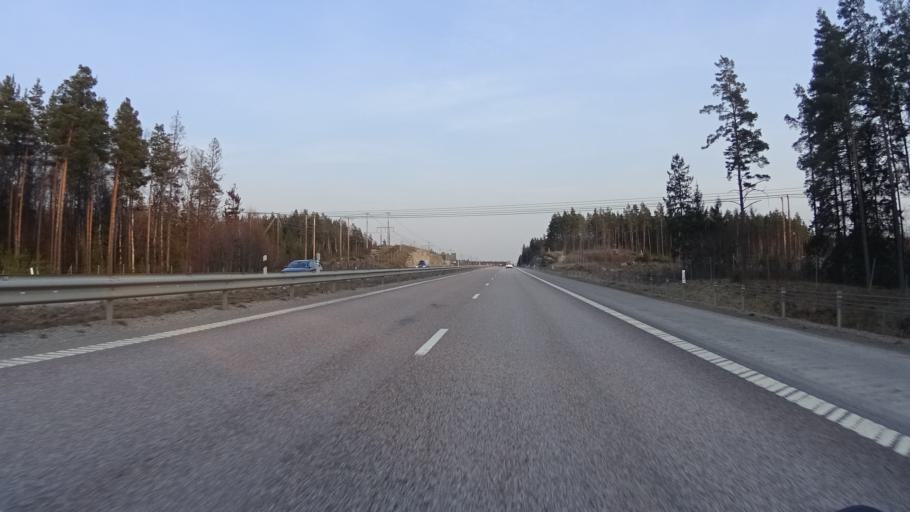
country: SE
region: Soedermanland
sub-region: Strangnas Kommun
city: Strangnas
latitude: 59.3253
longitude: 17.0295
